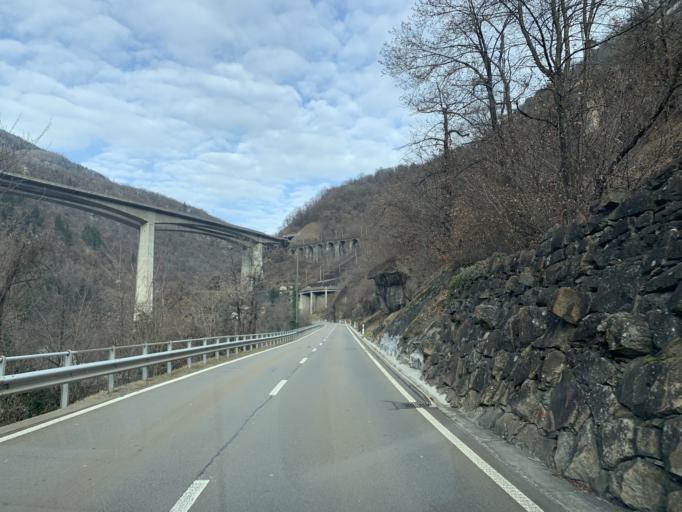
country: CH
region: Ticino
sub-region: Blenio District
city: Cancori
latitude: 46.4193
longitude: 8.8617
